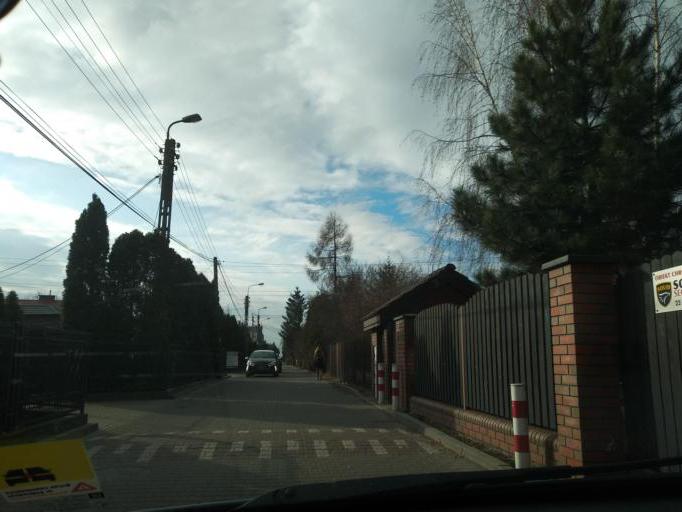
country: PL
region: Masovian Voivodeship
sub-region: Powiat piaseczynski
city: Mysiadlo
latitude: 52.0962
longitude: 21.0117
